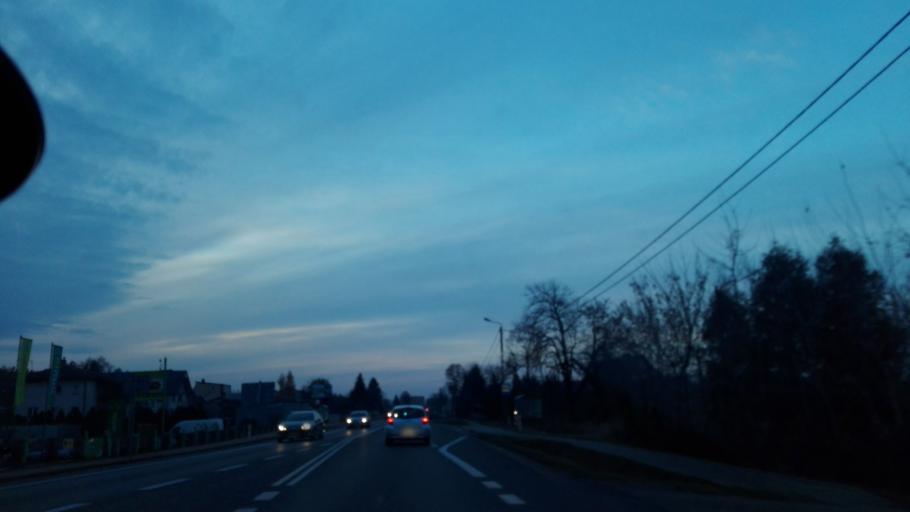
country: PL
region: Masovian Voivodeship
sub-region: Siedlce
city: Siedlce
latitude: 52.1733
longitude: 22.2105
